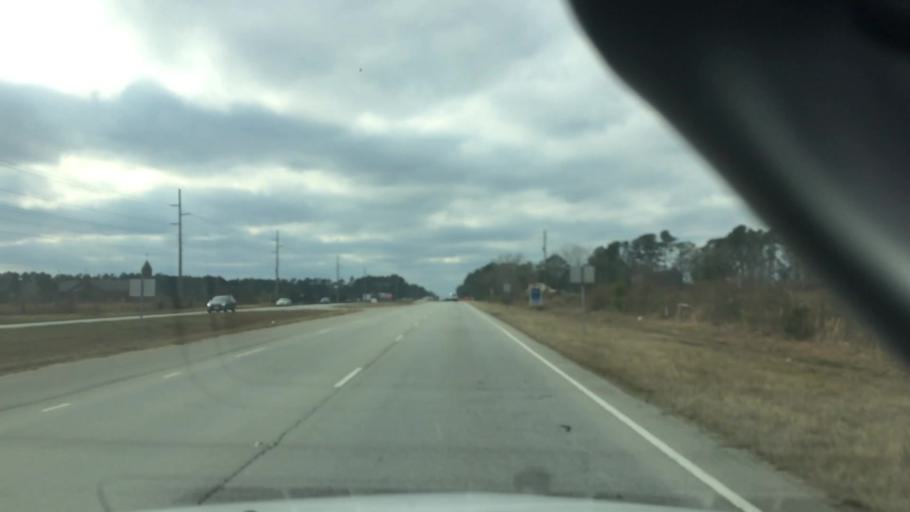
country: US
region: North Carolina
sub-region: Brunswick County
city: Shallotte
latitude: 33.9579
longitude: -78.4278
